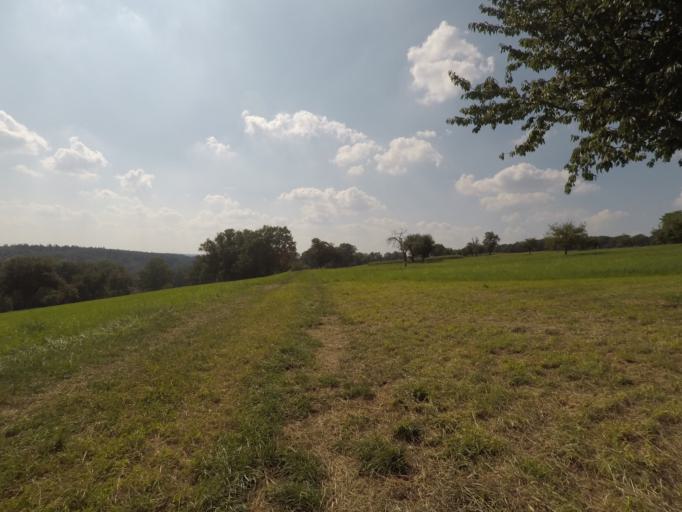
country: DE
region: Baden-Wuerttemberg
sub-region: Regierungsbezirk Stuttgart
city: Ostfildern
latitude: 48.7160
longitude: 9.2493
